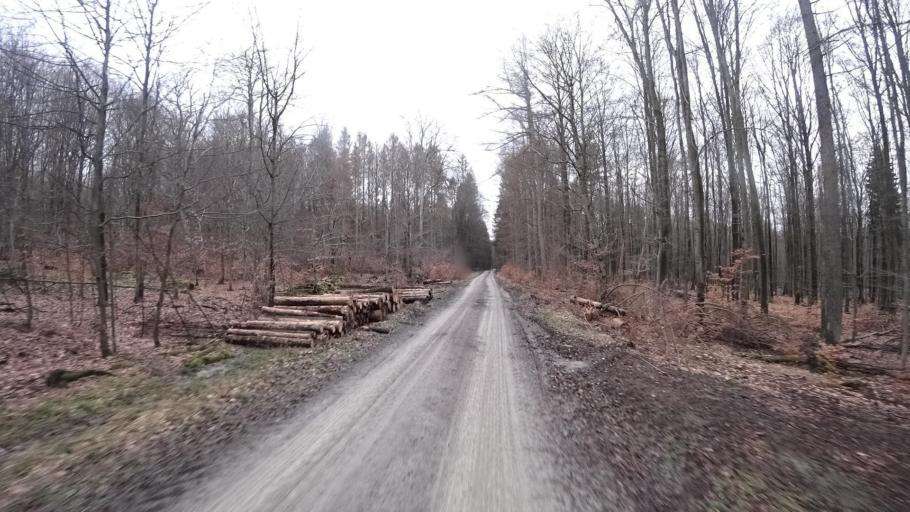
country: DE
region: Rheinland-Pfalz
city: Arzbach
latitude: 50.4171
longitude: 7.7631
